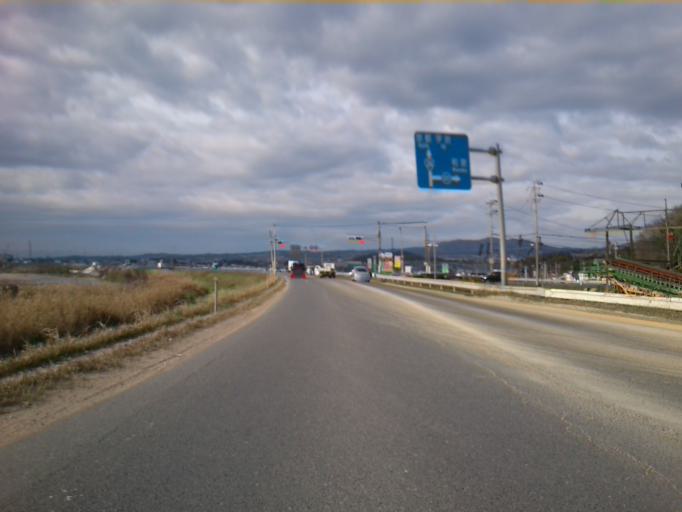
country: JP
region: Kyoto
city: Tanabe
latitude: 34.8065
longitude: 135.8052
